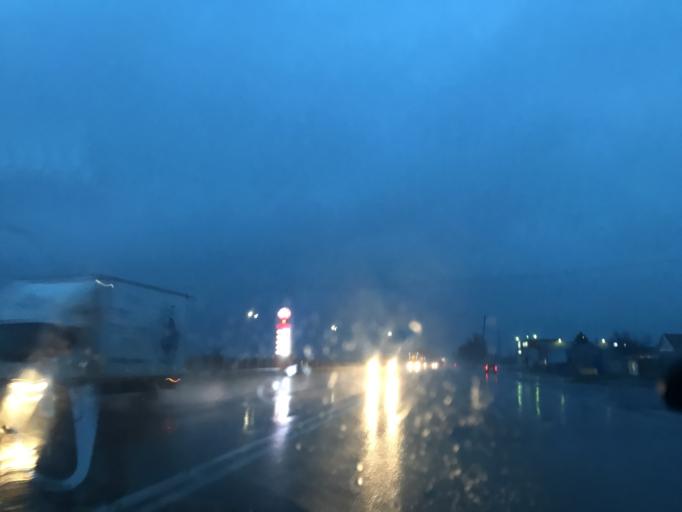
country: RU
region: Rostov
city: Bataysk
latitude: 47.0411
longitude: 39.7424
